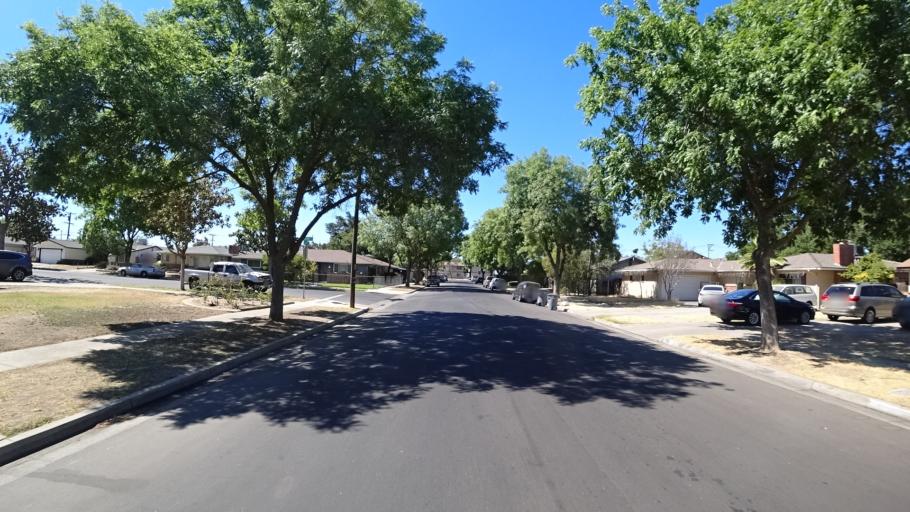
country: US
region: California
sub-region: Fresno County
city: Fresno
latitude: 36.7804
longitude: -119.8344
